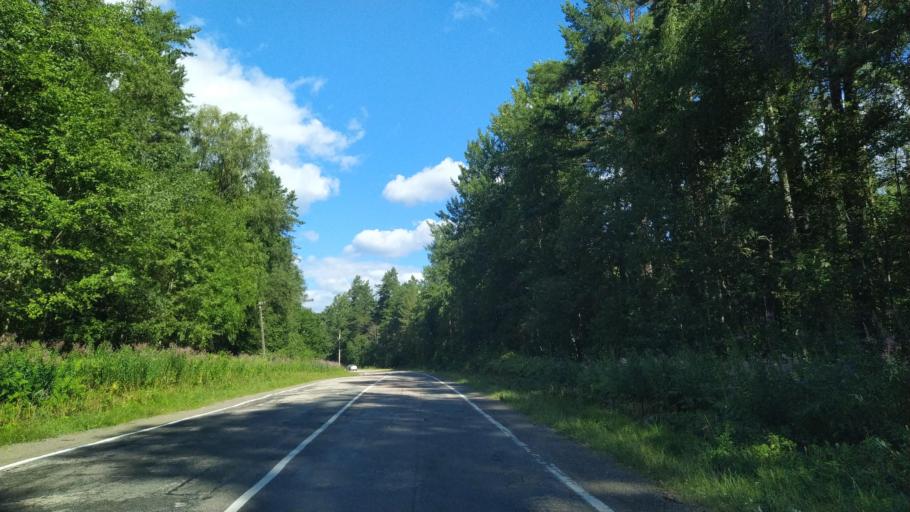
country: RU
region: Leningrad
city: Priozersk
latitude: 60.9724
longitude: 30.2820
